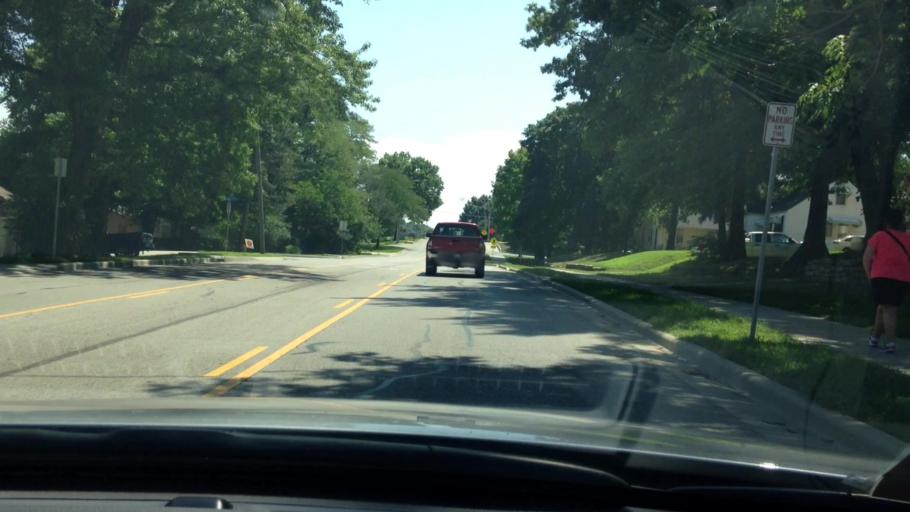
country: US
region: Kansas
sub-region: Johnson County
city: Mission
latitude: 39.0200
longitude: -94.6491
